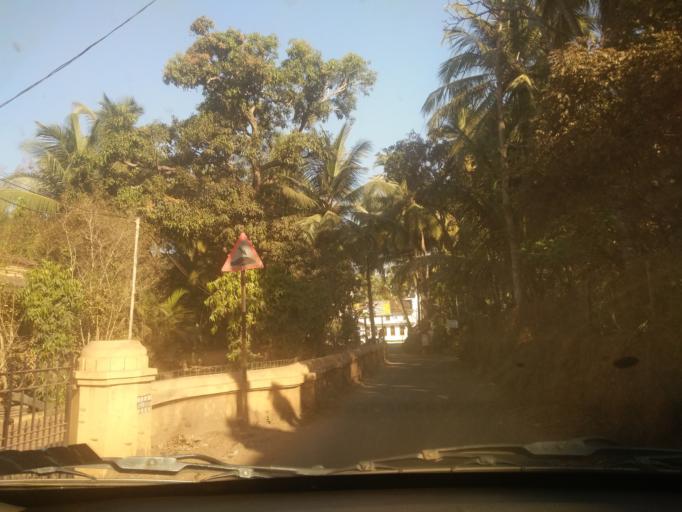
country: IN
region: Goa
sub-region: South Goa
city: Colva
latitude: 15.3125
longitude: 73.9102
